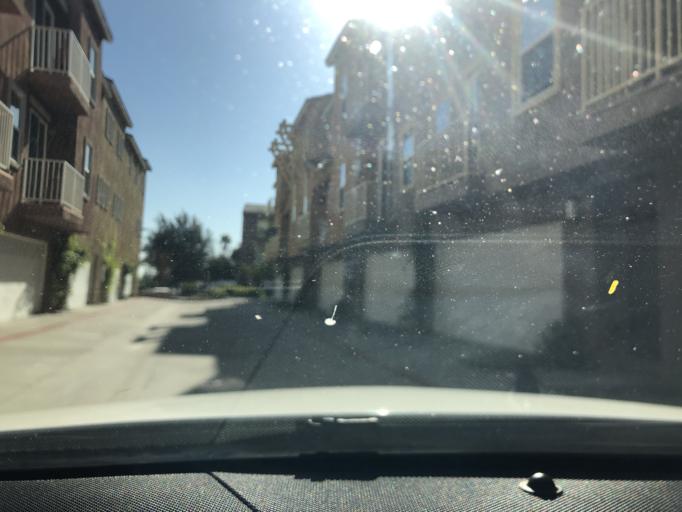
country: US
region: California
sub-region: San Diego County
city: Lemon Grove
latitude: 32.7398
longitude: -117.0576
